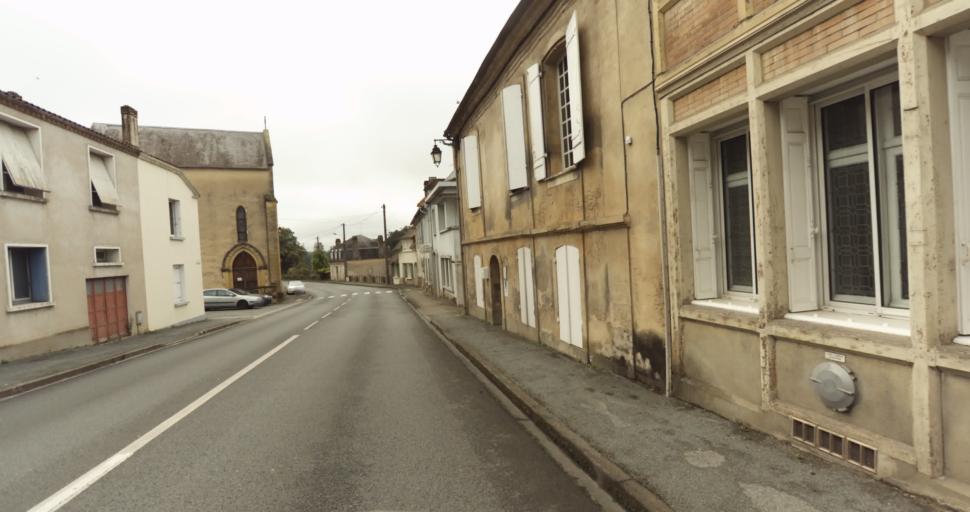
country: FR
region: Aquitaine
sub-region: Departement de la Dordogne
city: Mouleydier
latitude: 44.8547
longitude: 0.5954
